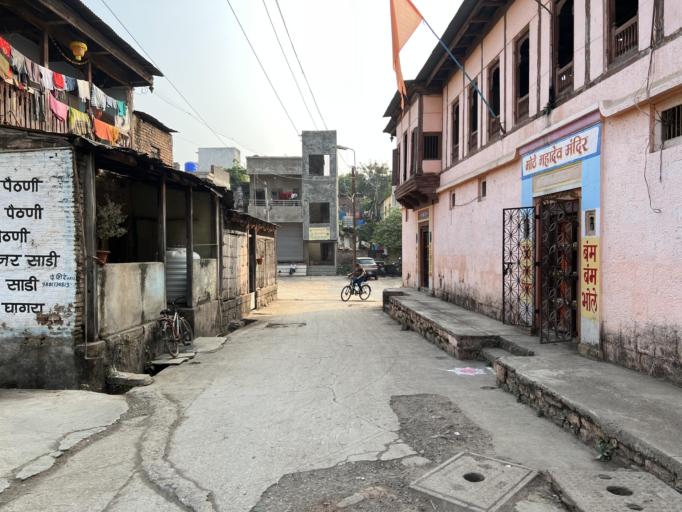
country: IN
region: Maharashtra
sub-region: Nashik Division
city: Yeola
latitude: 20.0413
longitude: 74.4889
